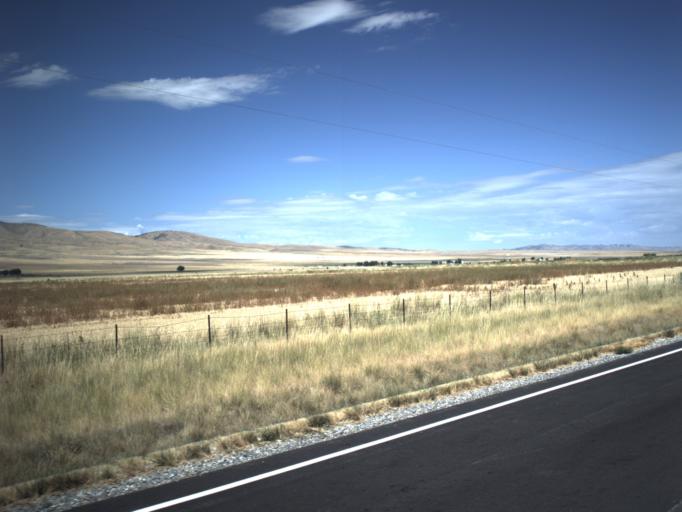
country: US
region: Utah
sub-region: Box Elder County
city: Garland
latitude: 41.7719
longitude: -112.4351
